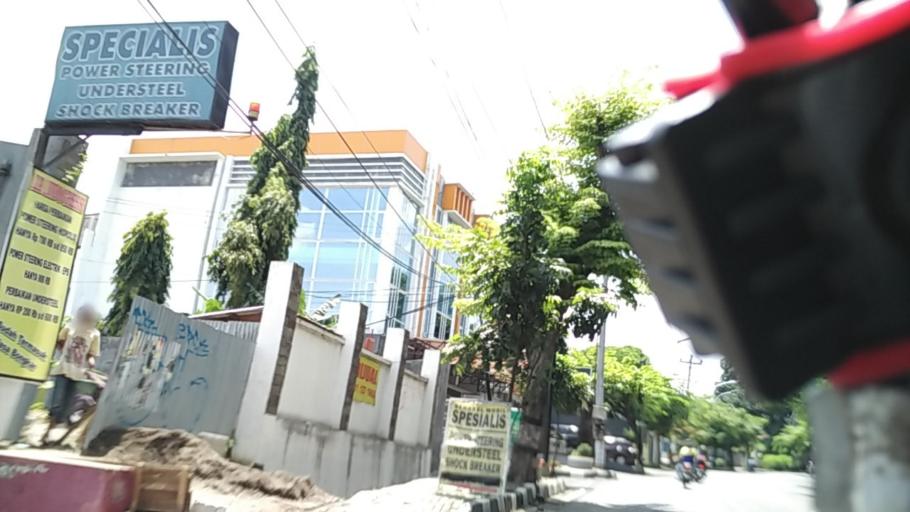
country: ID
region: Central Java
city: Semarang
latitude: -6.9896
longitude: 110.3824
